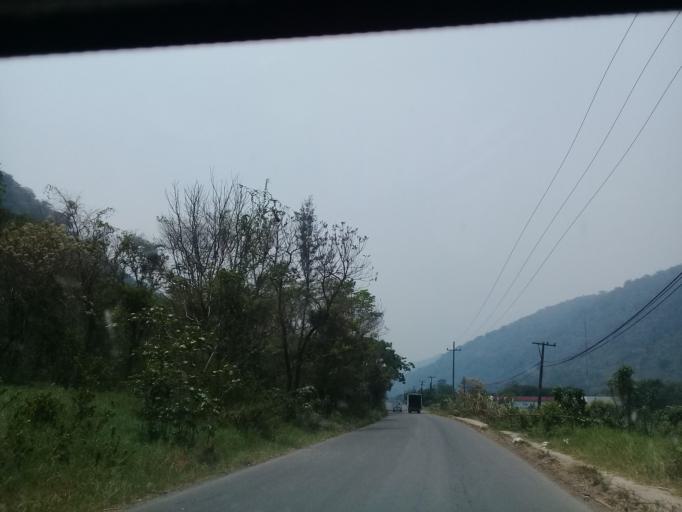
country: MX
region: Veracruz
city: Tezonapa
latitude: 18.6138
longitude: -96.6949
